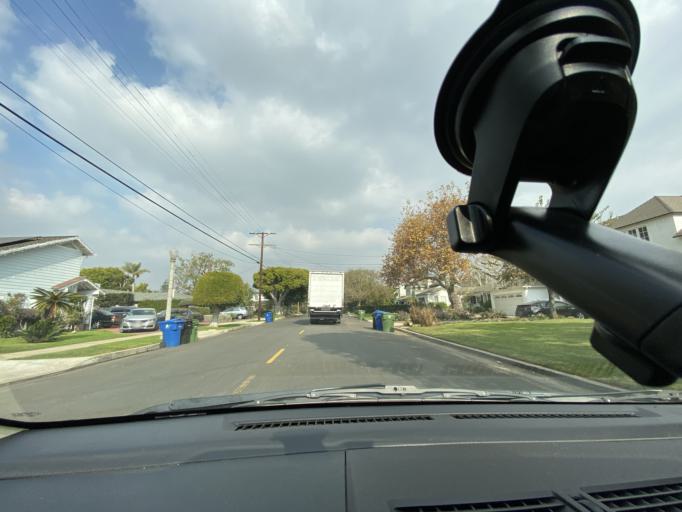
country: US
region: California
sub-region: Los Angeles County
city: Culver City
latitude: 34.0324
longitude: -118.4026
